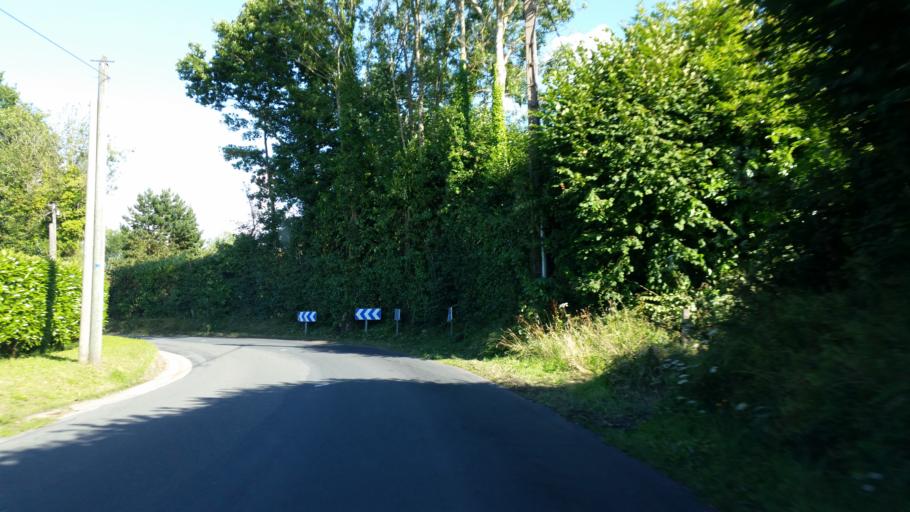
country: FR
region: Lower Normandy
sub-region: Departement du Calvados
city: Saint-Gatien-des-Bois
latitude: 49.3630
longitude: 0.1934
